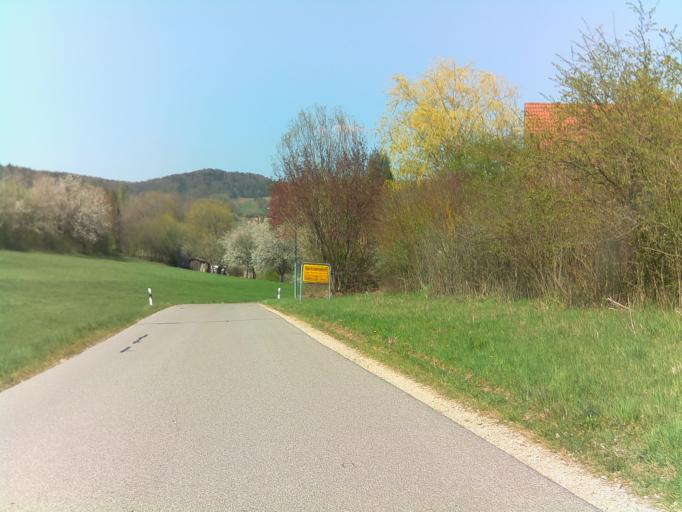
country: DE
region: Bavaria
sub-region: Upper Palatinate
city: Weigendorf
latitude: 49.4933
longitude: 11.5600
